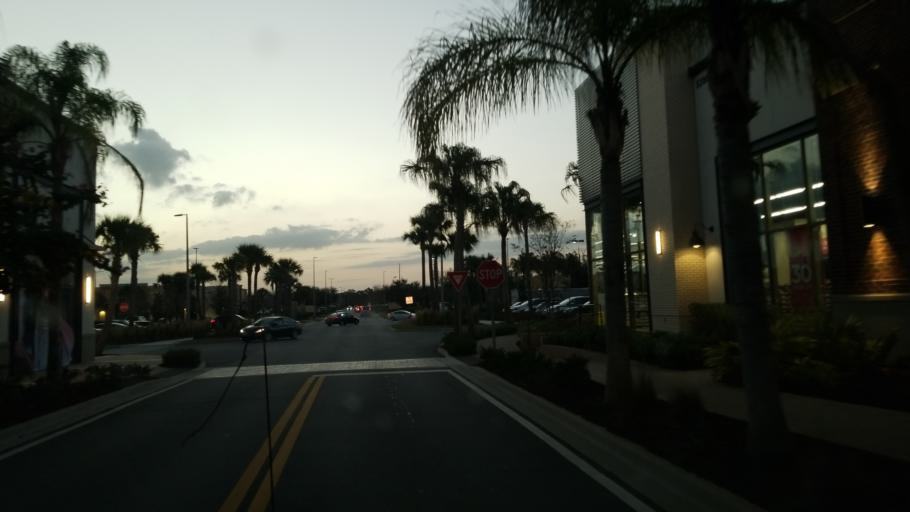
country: US
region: Florida
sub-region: Polk County
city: Citrus Ridge
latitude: 28.3459
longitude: -81.6093
